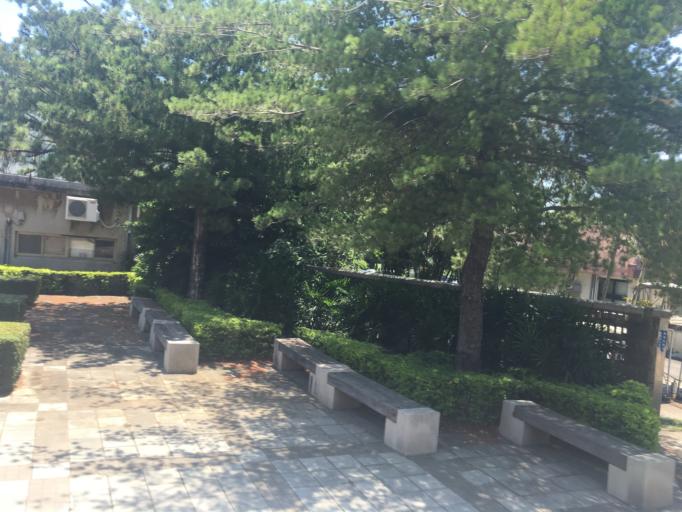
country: TW
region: Taiwan
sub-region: Hsinchu
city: Hsinchu
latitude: 24.7985
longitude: 120.9831
